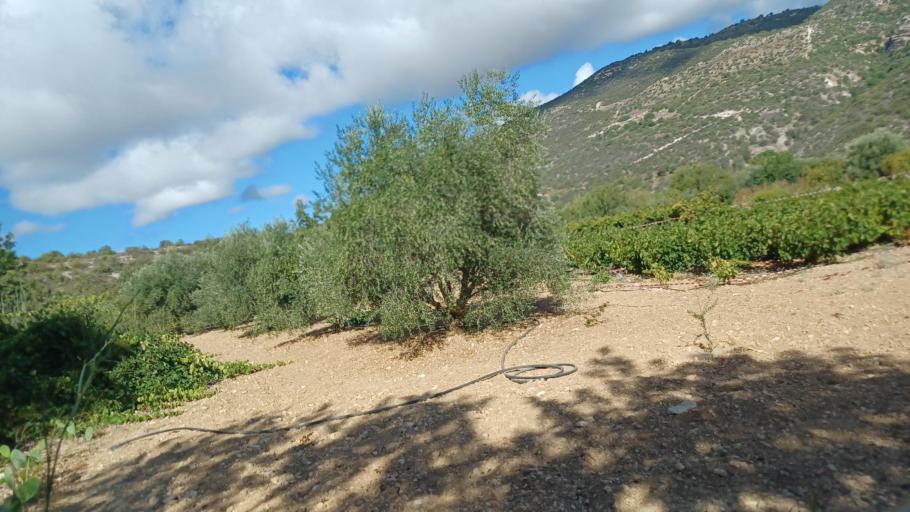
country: CY
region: Pafos
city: Tala
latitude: 34.8719
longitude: 32.4447
